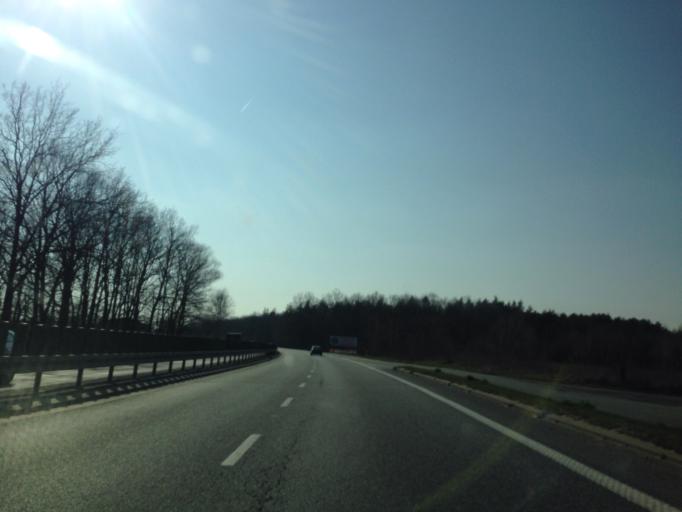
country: PL
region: Lower Silesian Voivodeship
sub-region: Powiat wroclawski
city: Dlugoleka
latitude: 51.1831
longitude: 17.2125
